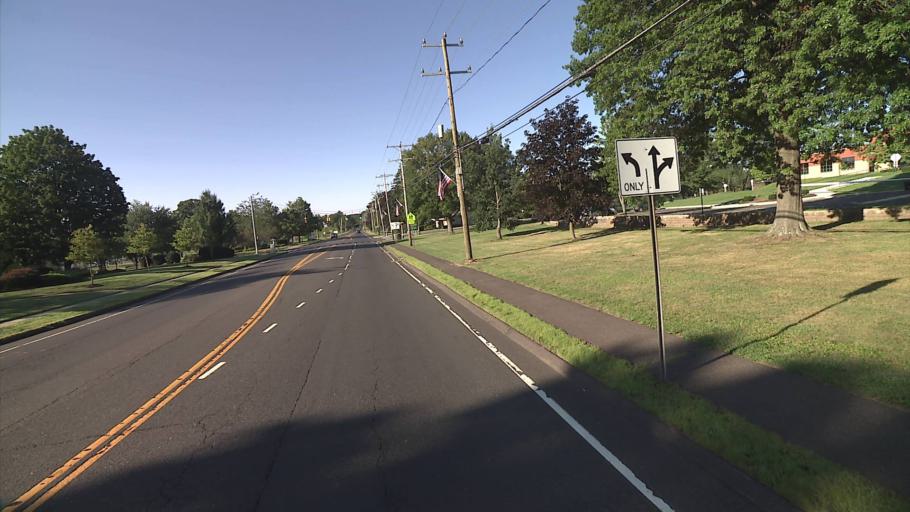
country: US
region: Connecticut
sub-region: New Haven County
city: Cheshire
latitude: 41.4900
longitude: -72.9047
